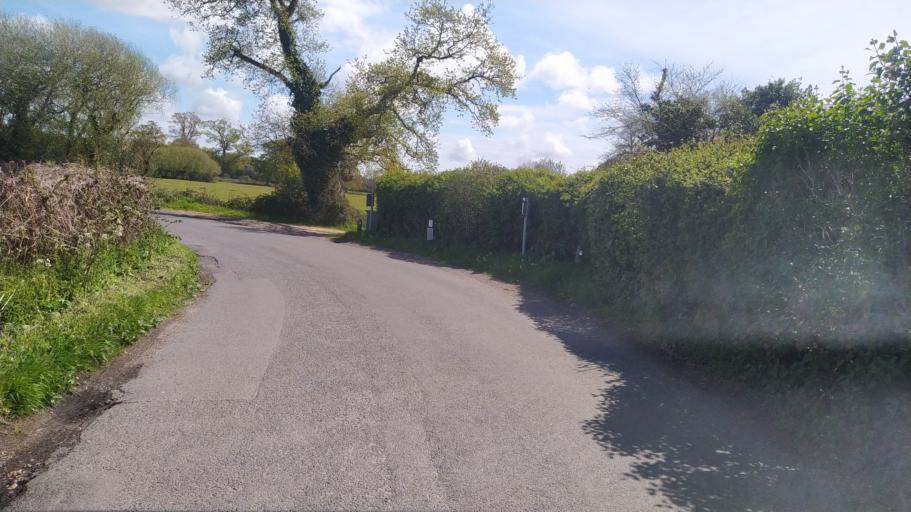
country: GB
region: England
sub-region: Hampshire
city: Fordingbridge
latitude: 50.8917
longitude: -1.8018
